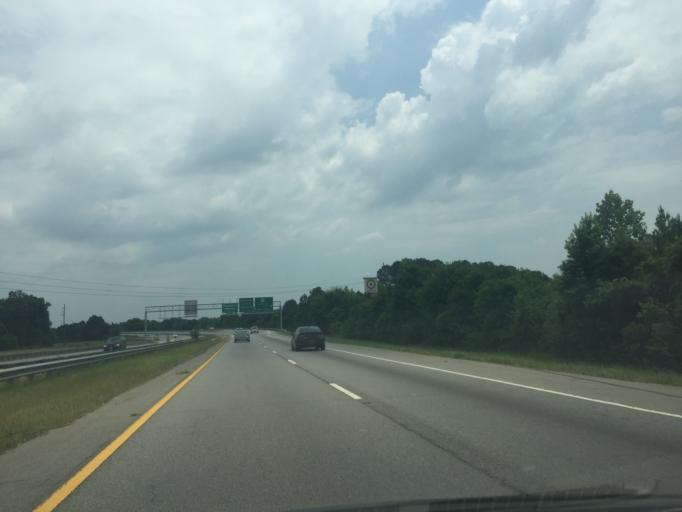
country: US
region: Georgia
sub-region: Chatham County
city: Thunderbolt
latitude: 32.0390
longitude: -81.0740
